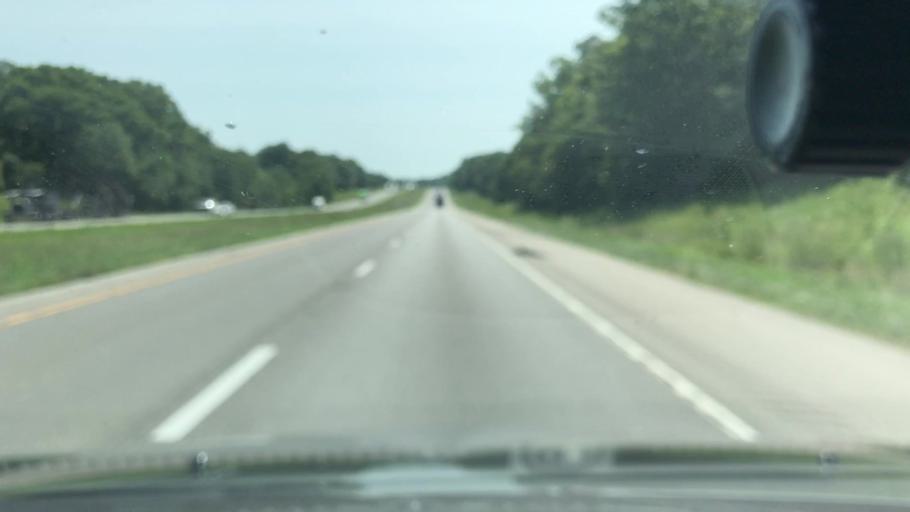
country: US
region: Illinois
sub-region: Clinton County
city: Wamac
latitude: 38.3715
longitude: -89.0967
